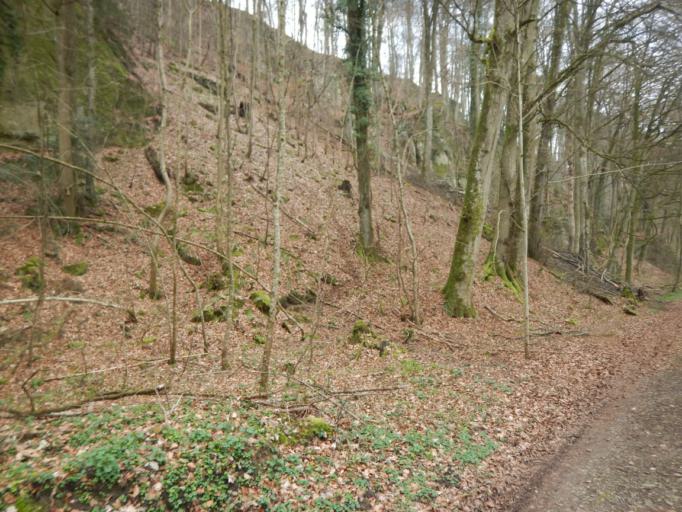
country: LU
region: Grevenmacher
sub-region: Canton d'Echternach
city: Beaufort
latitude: 49.8380
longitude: 6.3178
